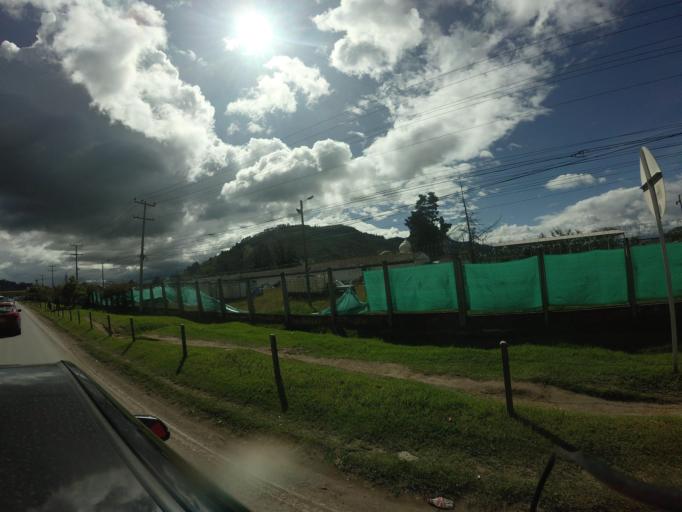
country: CO
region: Cundinamarca
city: Sopo
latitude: 4.9432
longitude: -73.9590
